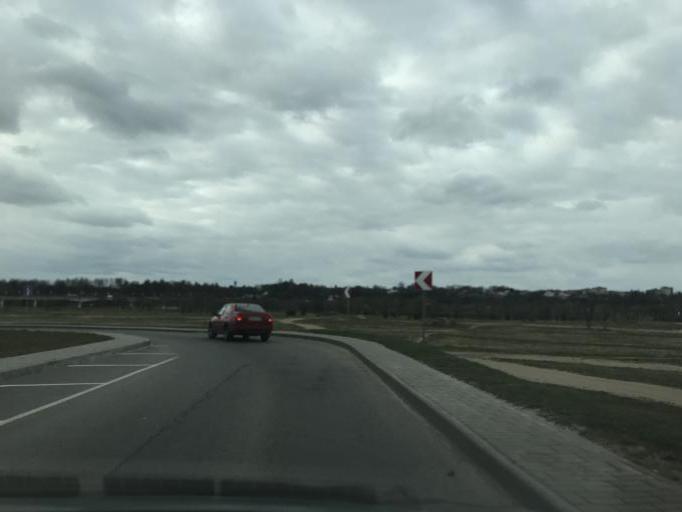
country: BY
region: Mogilev
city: Mahilyow
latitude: 53.8817
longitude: 30.3203
